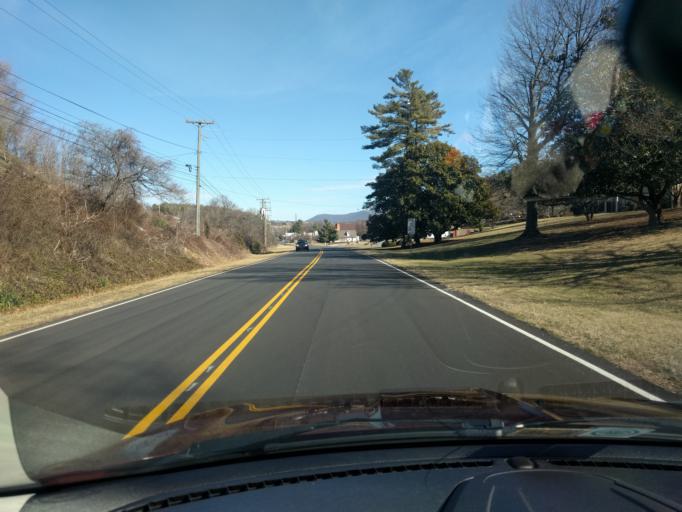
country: US
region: Virginia
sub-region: Roanoke County
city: Vinton
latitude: 37.3183
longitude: -79.8752
